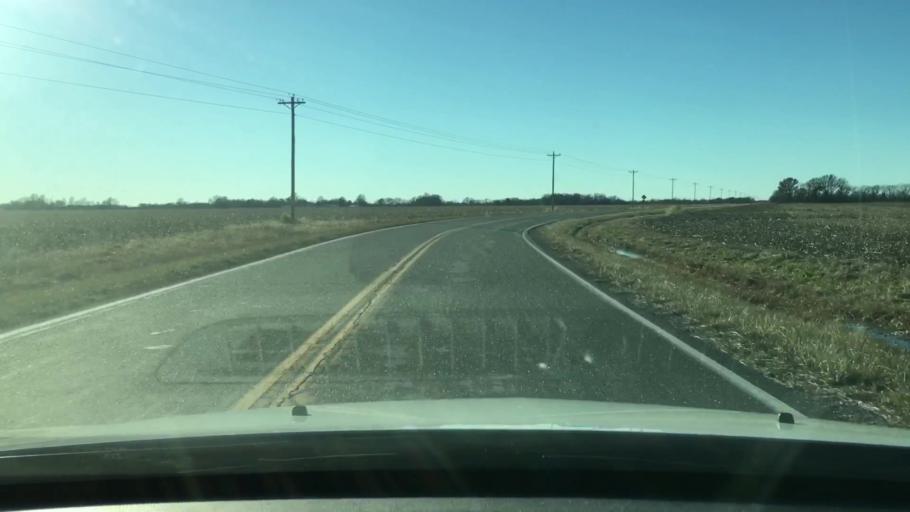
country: US
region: Missouri
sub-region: Audrain County
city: Mexico
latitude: 39.2812
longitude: -91.7399
